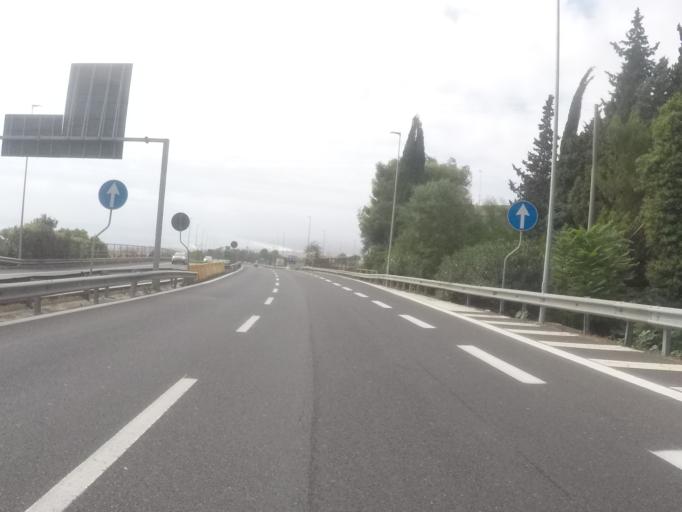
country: IT
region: Sicily
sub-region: Catania
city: Carrubazza-Motta
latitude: 37.5529
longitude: 15.0986
